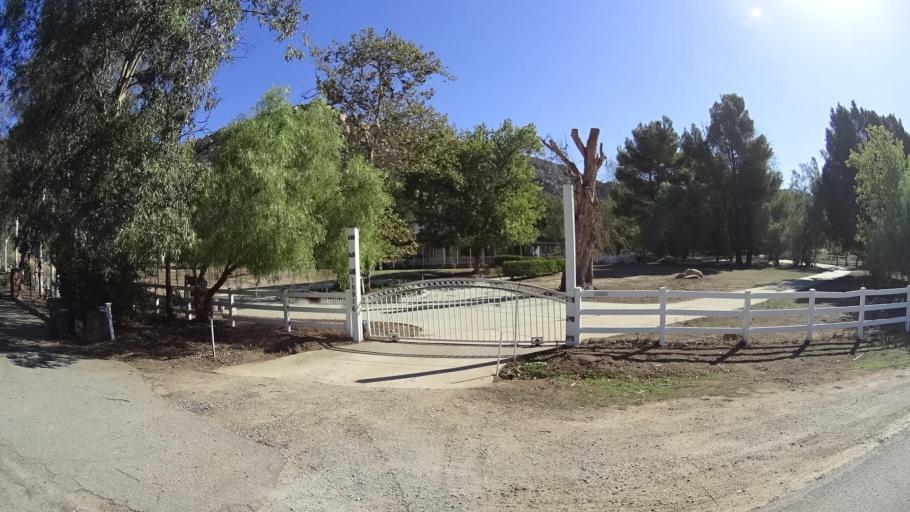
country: US
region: California
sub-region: San Diego County
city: Jamul
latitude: 32.7190
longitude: -116.8034
